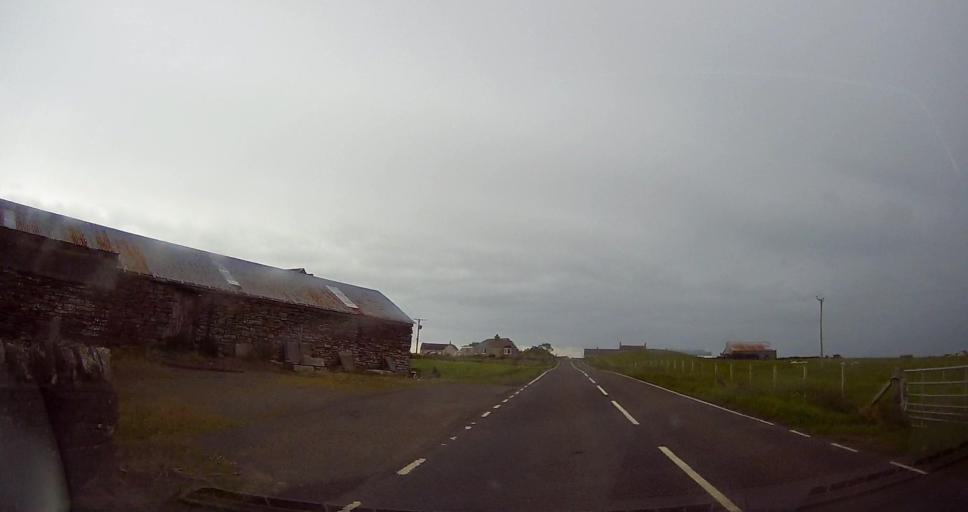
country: GB
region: Scotland
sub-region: Orkney Islands
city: Stromness
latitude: 59.0293
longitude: -3.1770
